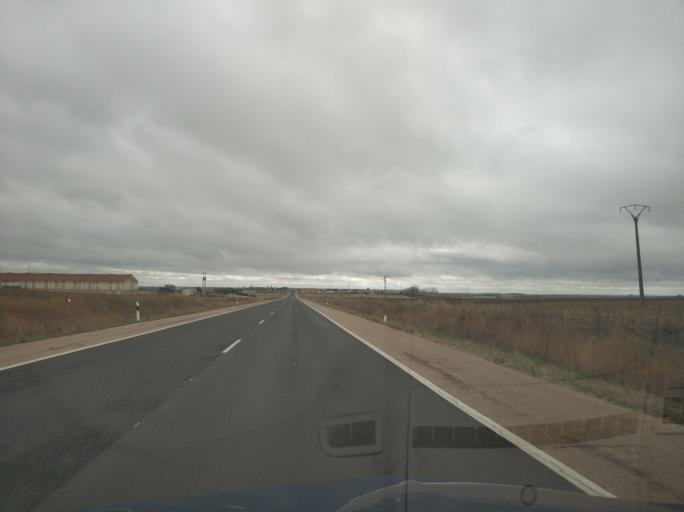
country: ES
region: Castille and Leon
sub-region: Provincia de Salamanca
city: Villaverde de Guarena
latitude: 41.0705
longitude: -5.5348
